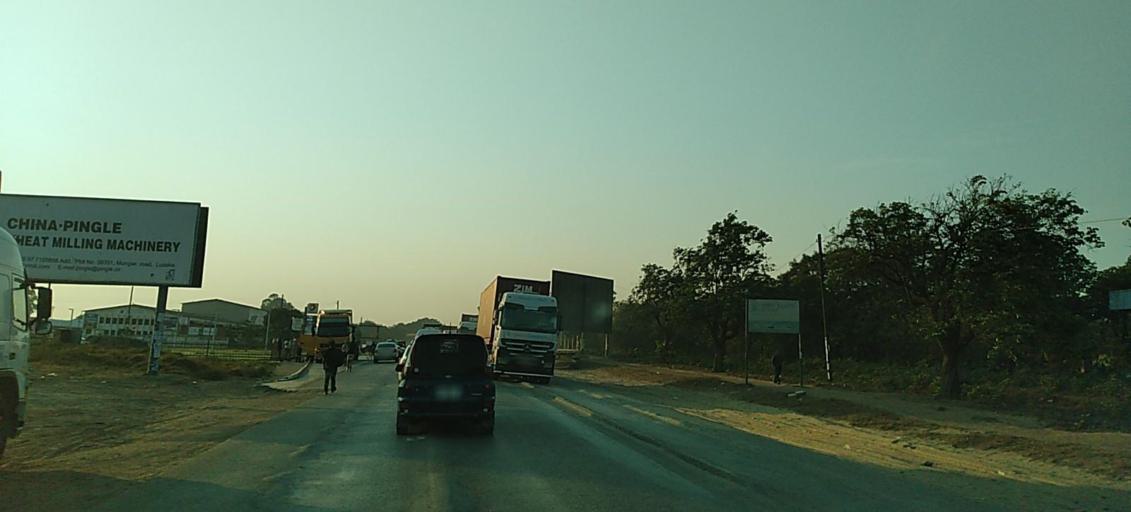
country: ZM
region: Copperbelt
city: Ndola
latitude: -13.0075
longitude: 28.6527
